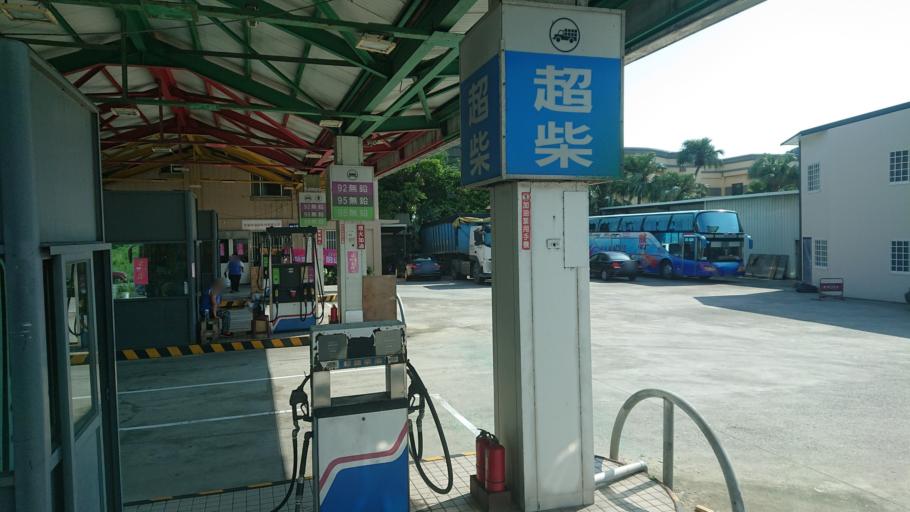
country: TW
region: Taiwan
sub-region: Miaoli
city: Miaoli
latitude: 24.6015
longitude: 120.7801
